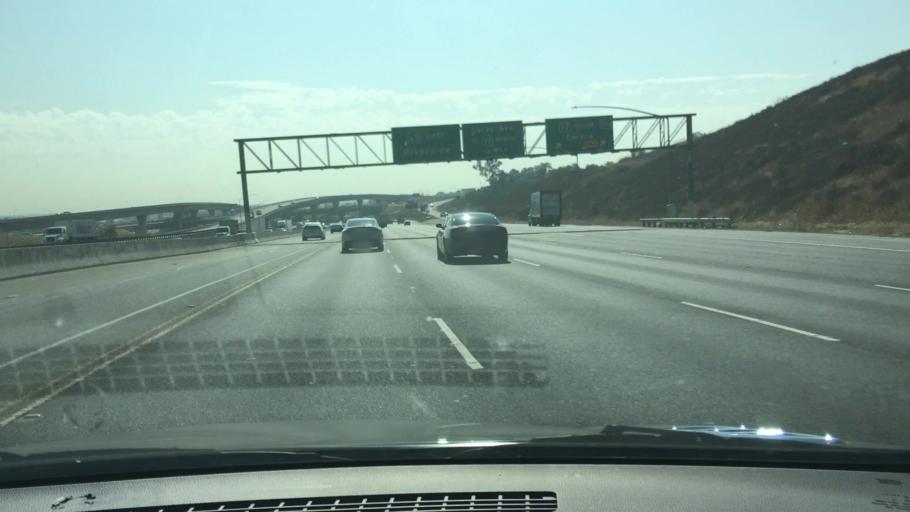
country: US
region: California
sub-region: San Bernardino County
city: Chino Hills
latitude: 34.0245
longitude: -117.7561
